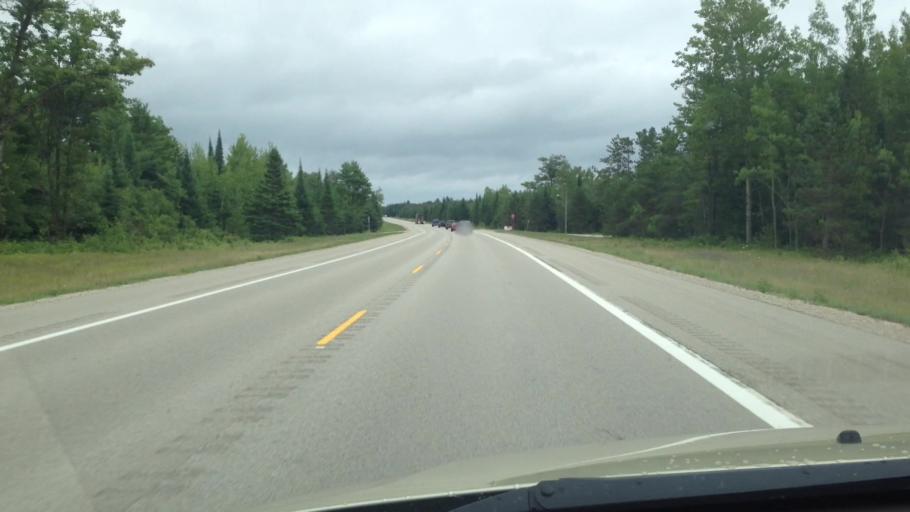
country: US
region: Michigan
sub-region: Schoolcraft County
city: Manistique
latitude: 45.9036
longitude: -86.3761
